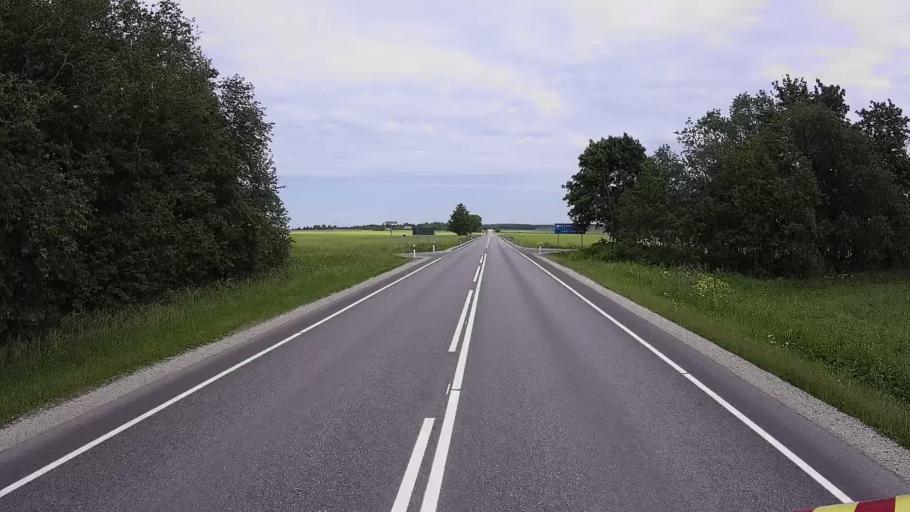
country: EE
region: Laeaene-Virumaa
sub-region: Rakvere linn
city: Rakvere
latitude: 59.2956
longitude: 26.3122
